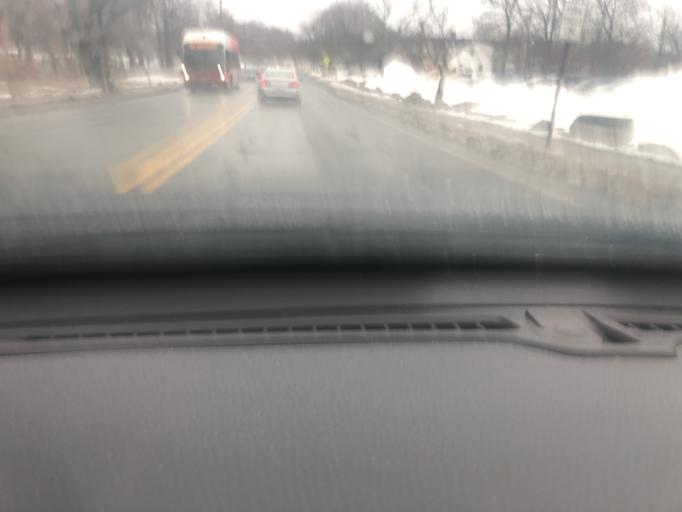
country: US
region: Massachusetts
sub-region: Norfolk County
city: Avon
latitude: 42.1017
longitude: -71.0499
